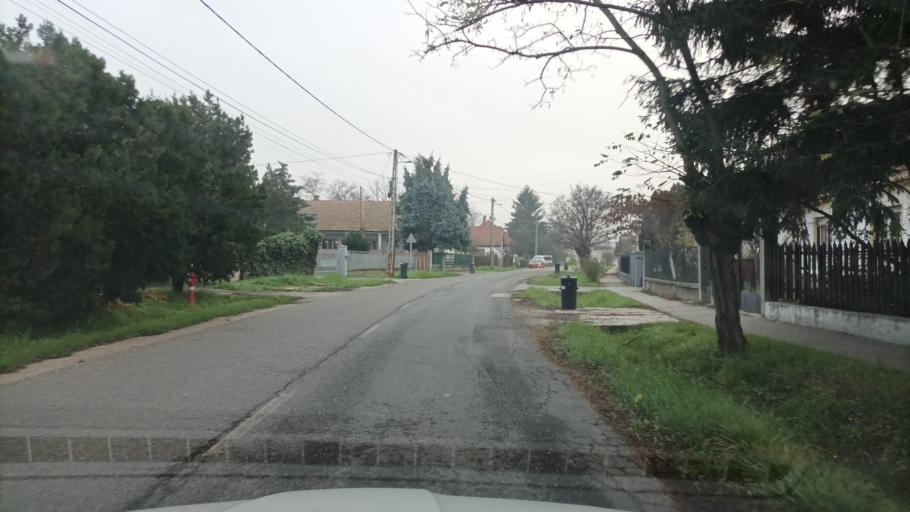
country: HU
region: Pest
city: Toekoel
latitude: 47.3171
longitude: 18.9709
